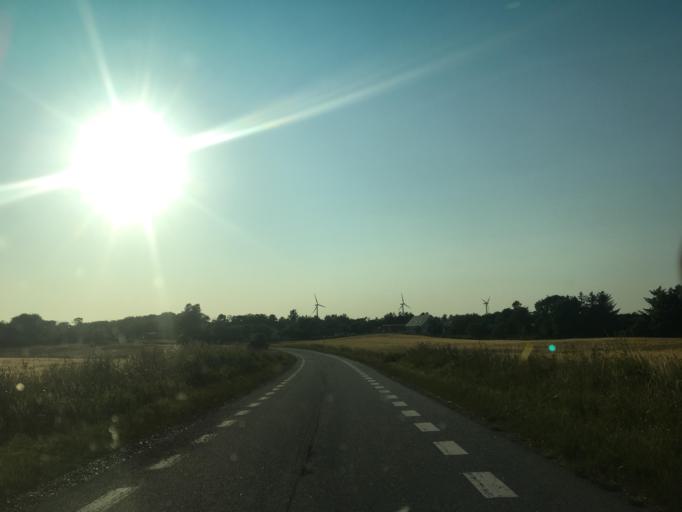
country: DK
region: North Denmark
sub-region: Thisted Kommune
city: Hurup
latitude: 56.8201
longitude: 8.3639
